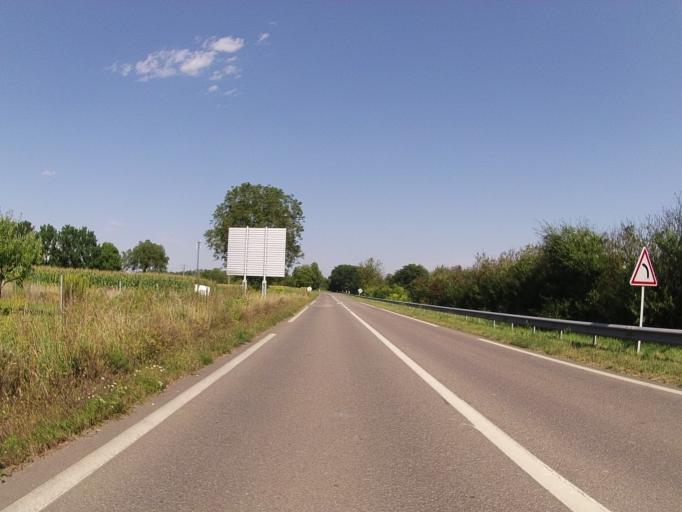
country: FR
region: Alsace
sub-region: Departement du Bas-Rhin
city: Seltz
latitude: 48.9244
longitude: 8.1418
